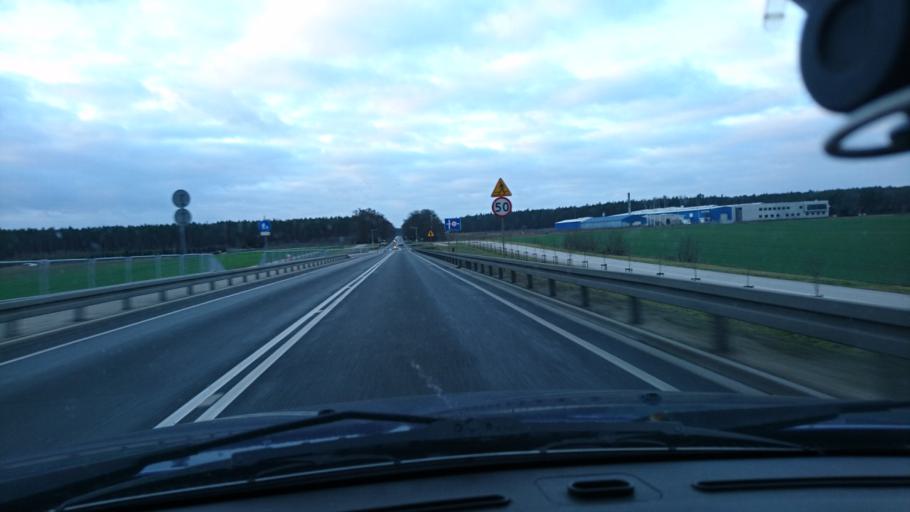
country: PL
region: Greater Poland Voivodeship
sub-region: Powiat kepinski
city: Kepno
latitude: 51.3184
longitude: 17.9773
